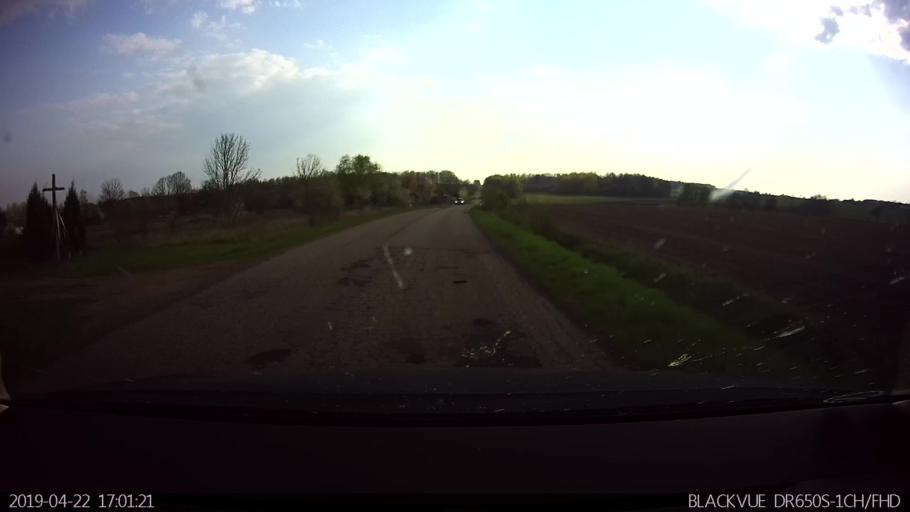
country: PL
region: Podlasie
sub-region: Powiat siemiatycki
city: Drohiczyn
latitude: 52.4388
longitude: 22.7190
